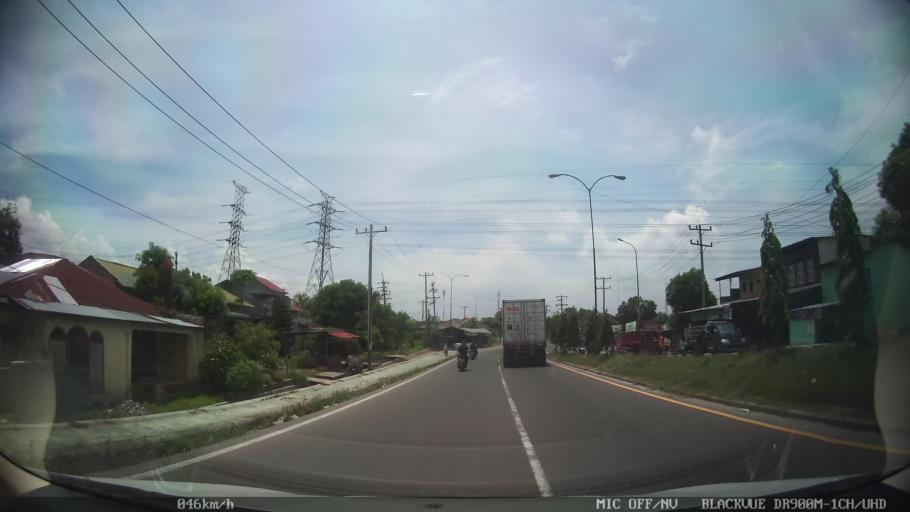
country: ID
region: North Sumatra
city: Belawan
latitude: 3.7566
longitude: 98.6771
